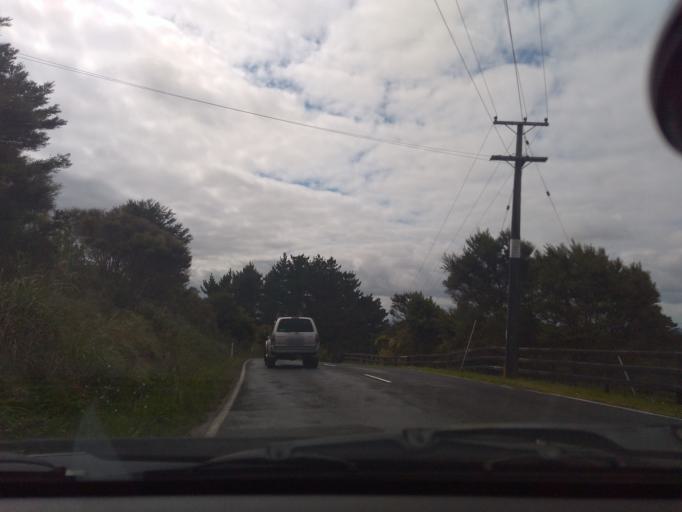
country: NZ
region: Auckland
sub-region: Auckland
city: Muriwai Beach
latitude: -36.8519
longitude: 174.5140
